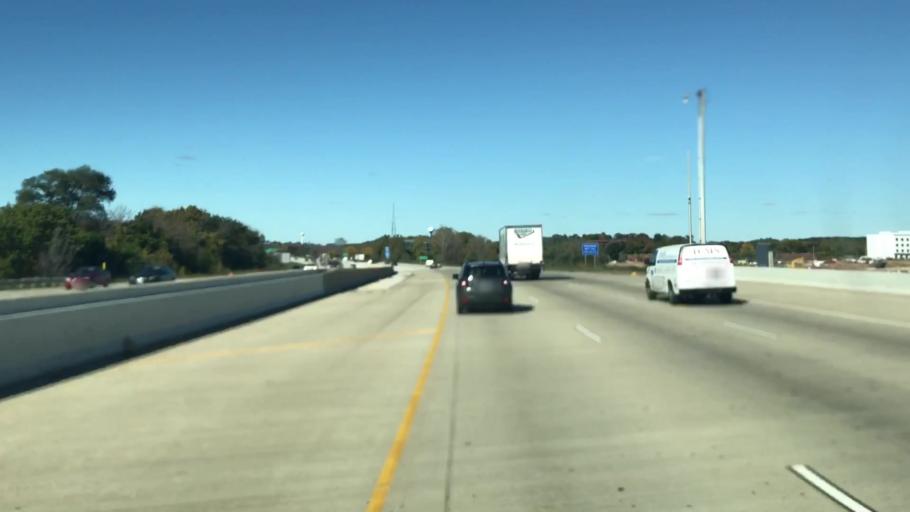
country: US
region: Wisconsin
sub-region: Waukesha County
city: Brookfield
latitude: 43.0282
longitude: -88.1271
